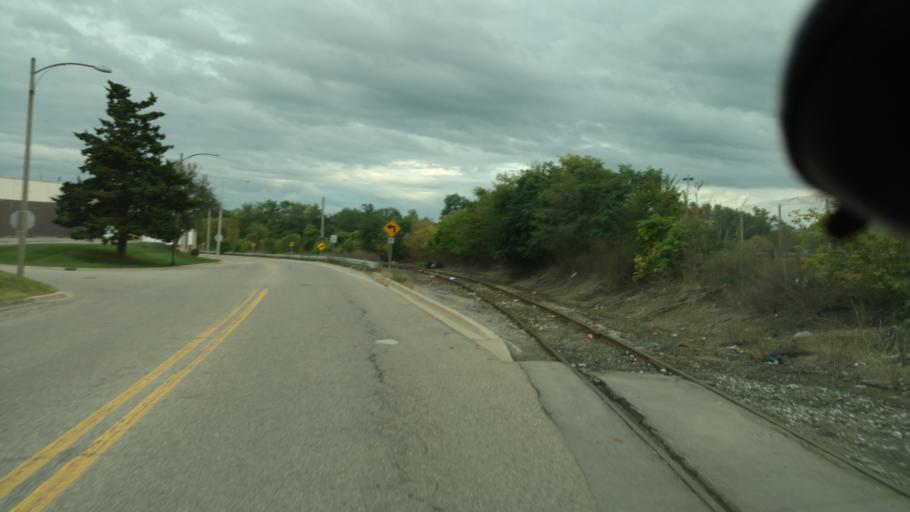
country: US
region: Michigan
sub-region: Ingham County
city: Edgemont Park
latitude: 42.7246
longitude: -84.5818
